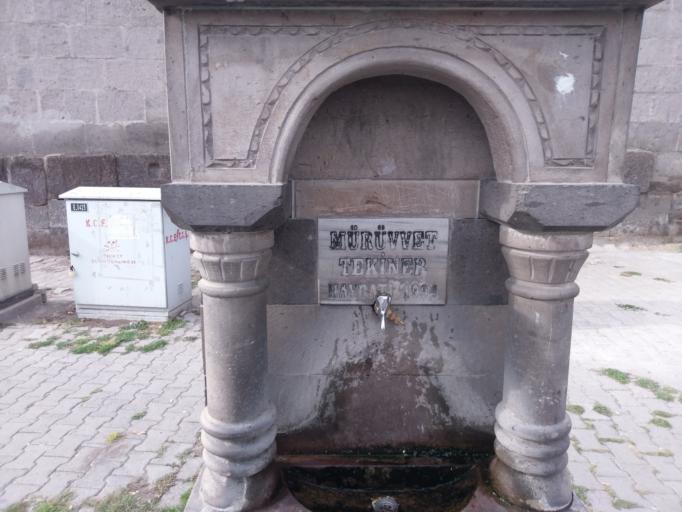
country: TR
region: Kayseri
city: Kayseri
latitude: 38.7174
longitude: 35.4906
